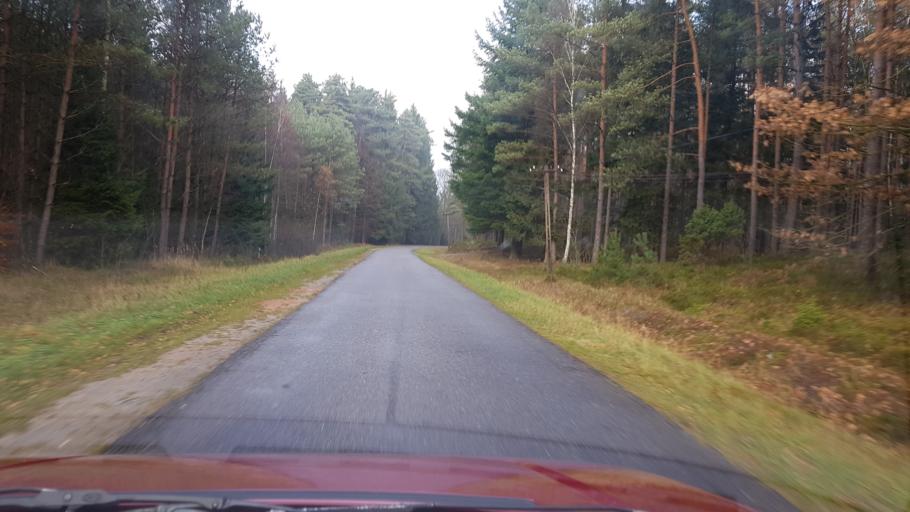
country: PL
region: West Pomeranian Voivodeship
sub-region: Powiat bialogardzki
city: Tychowo
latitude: 53.9561
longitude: 16.3165
